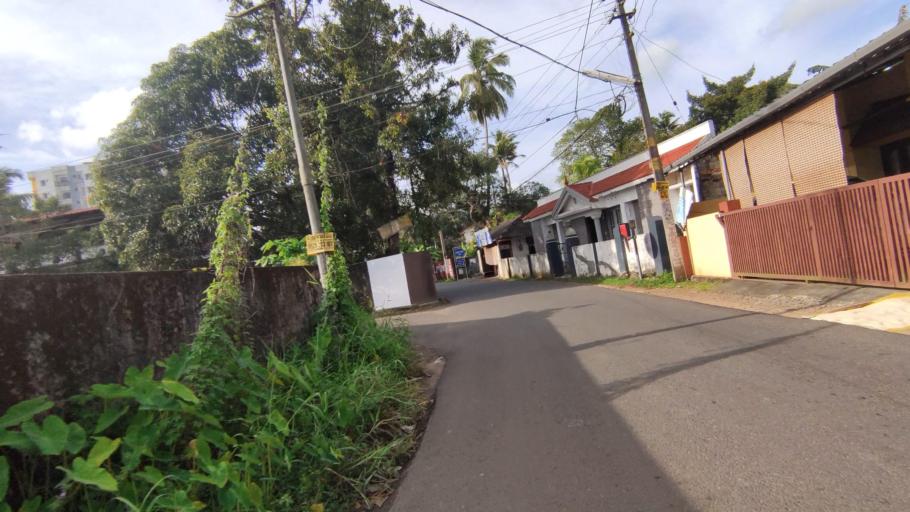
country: IN
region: Kerala
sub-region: Kottayam
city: Kottayam
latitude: 9.5796
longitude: 76.4992
